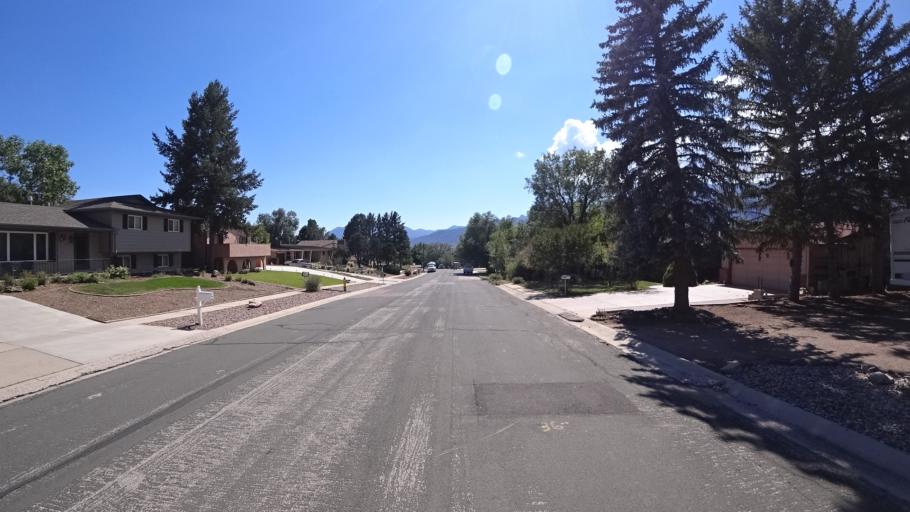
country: US
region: Colorado
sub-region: El Paso County
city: Colorado Springs
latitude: 38.8592
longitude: -104.8611
